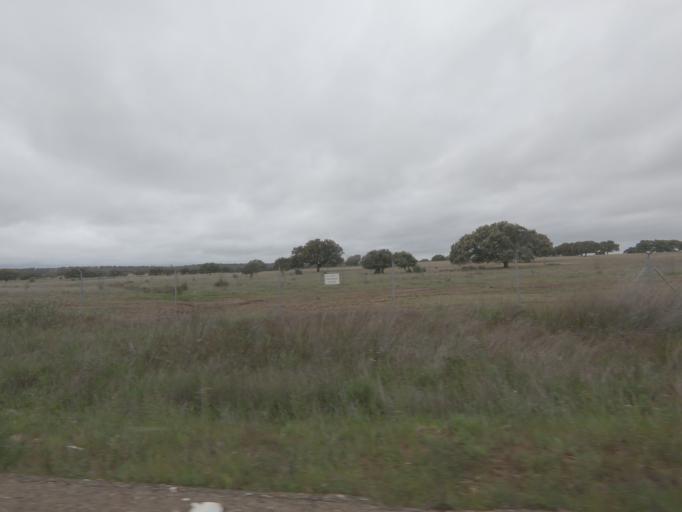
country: ES
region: Extremadura
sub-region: Provincia de Badajoz
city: Villar del Rey
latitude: 39.0185
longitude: -6.8491
